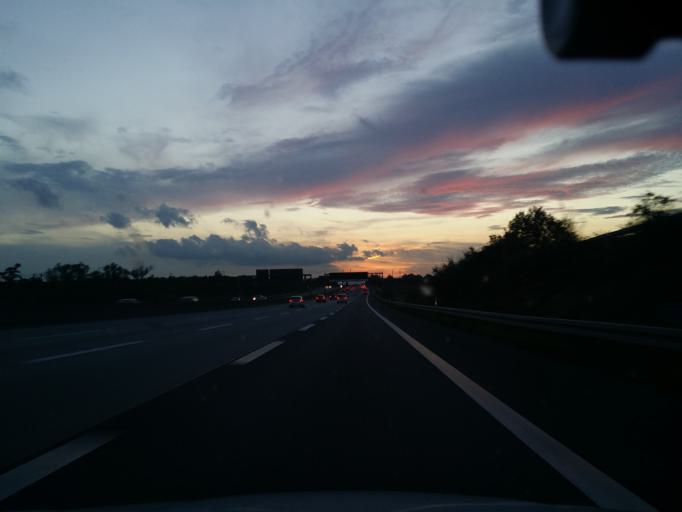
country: DE
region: Hesse
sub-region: Regierungsbezirk Darmstadt
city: Florsheim
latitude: 50.0557
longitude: 8.4007
